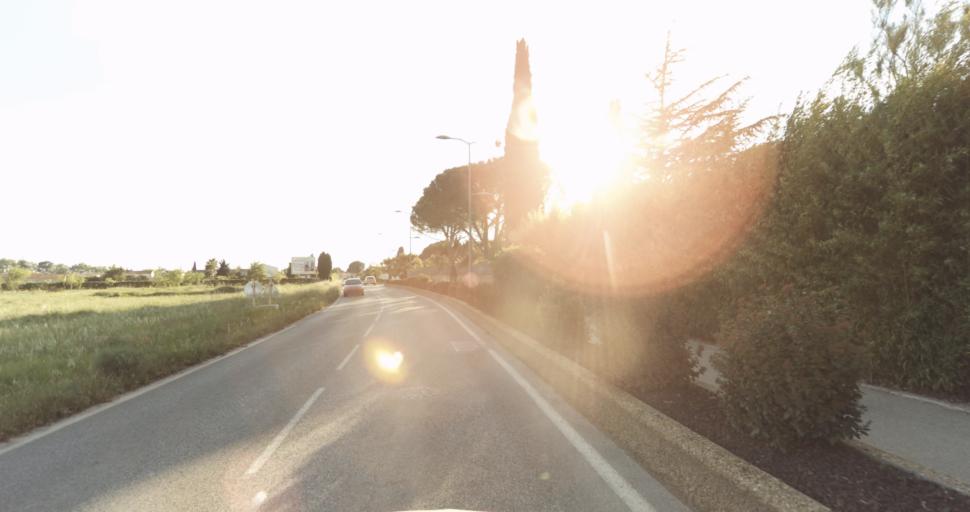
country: FR
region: Provence-Alpes-Cote d'Azur
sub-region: Departement du Var
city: La Crau
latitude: 43.1543
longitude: 6.0881
